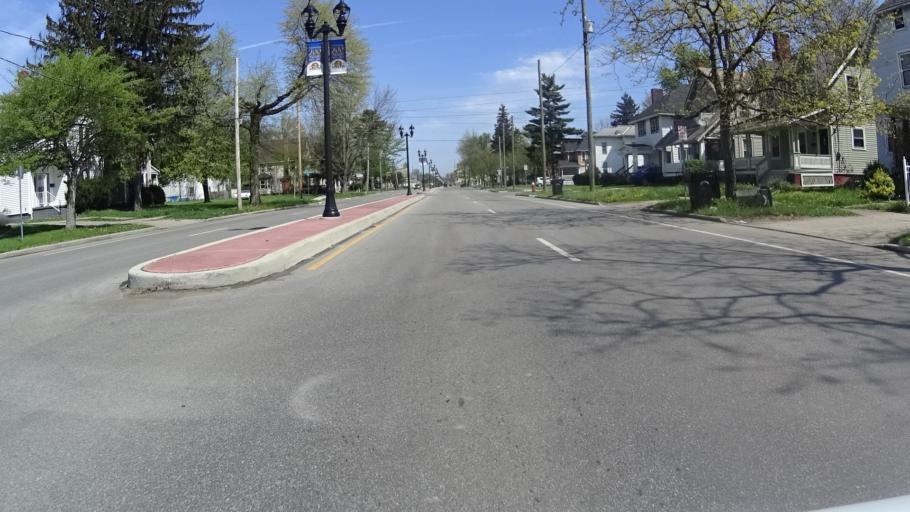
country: US
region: Ohio
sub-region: Lorain County
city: Elyria
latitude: 41.3562
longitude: -82.1073
